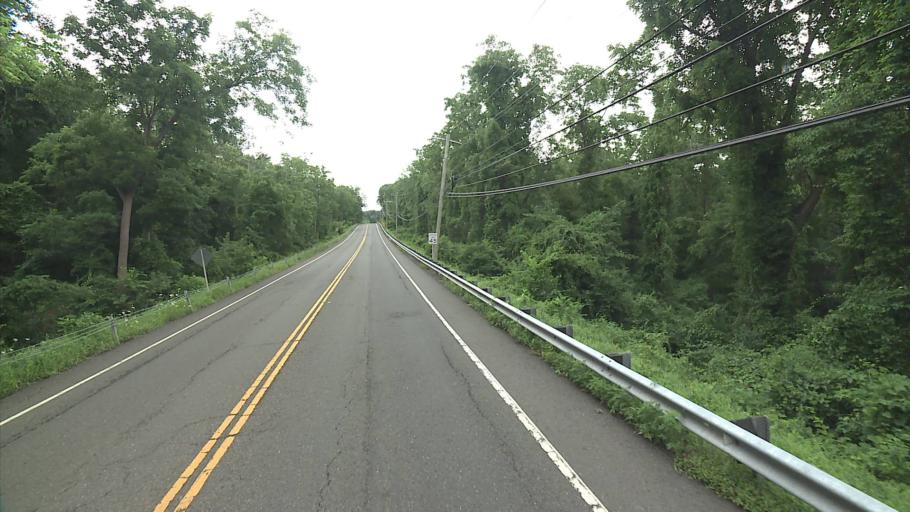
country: US
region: Connecticut
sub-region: Litchfield County
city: New Milford
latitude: 41.5521
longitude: -73.3828
